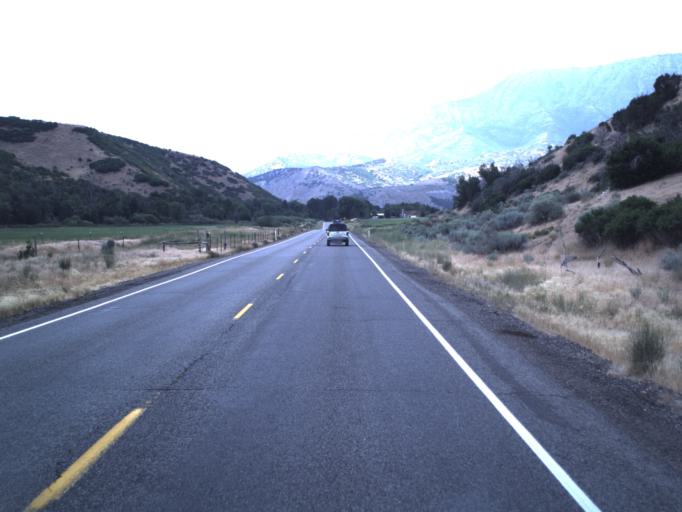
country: US
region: Utah
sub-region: Sanpete County
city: Fountain Green
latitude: 39.7051
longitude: -111.7093
